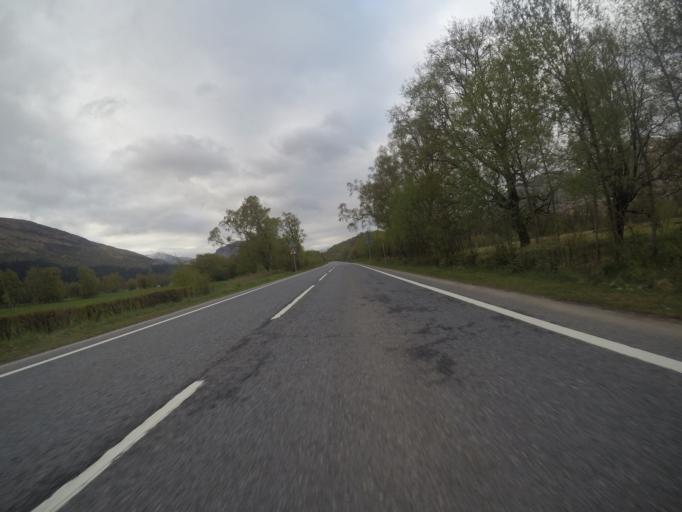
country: GB
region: Scotland
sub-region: Highland
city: Spean Bridge
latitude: 56.9510
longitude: -4.4960
